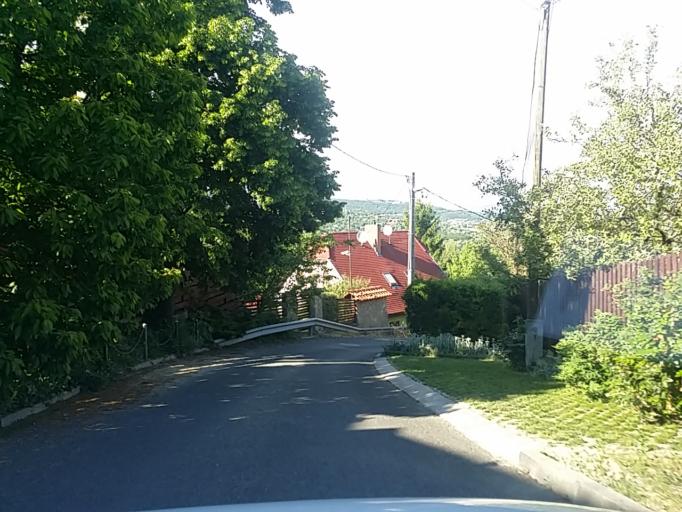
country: HU
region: Budapest
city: Budapest III. keruelet
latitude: 47.5583
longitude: 19.0180
